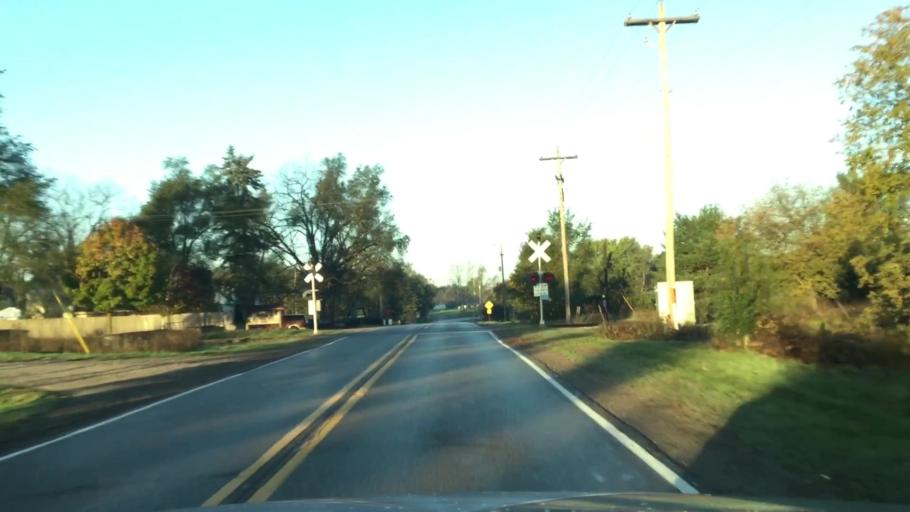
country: US
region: Michigan
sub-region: Livingston County
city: Howell
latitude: 42.6981
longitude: -83.9421
